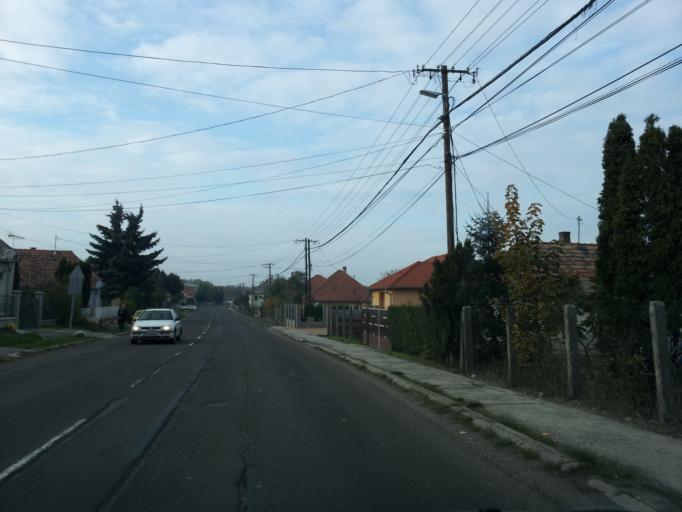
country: HU
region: Gyor-Moson-Sopron
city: Pannonhalma
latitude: 47.5185
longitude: 17.7525
